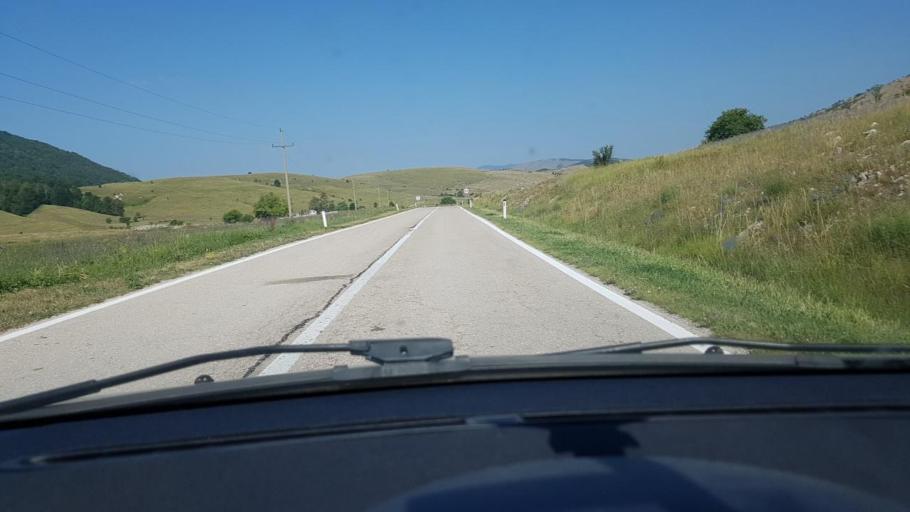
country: BA
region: Federation of Bosnia and Herzegovina
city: Bosansko Grahovo
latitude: 44.1257
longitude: 16.5218
